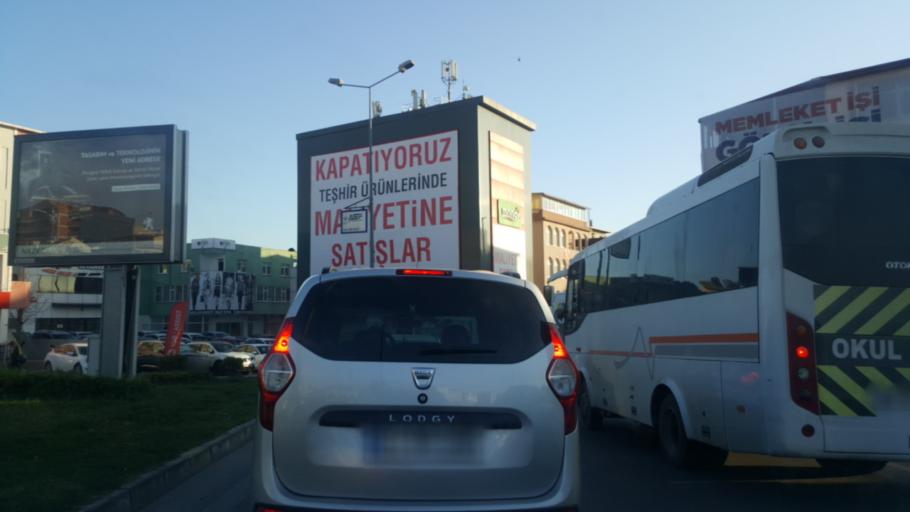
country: TR
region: Kocaeli
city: Darica
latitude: 40.7855
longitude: 29.4157
